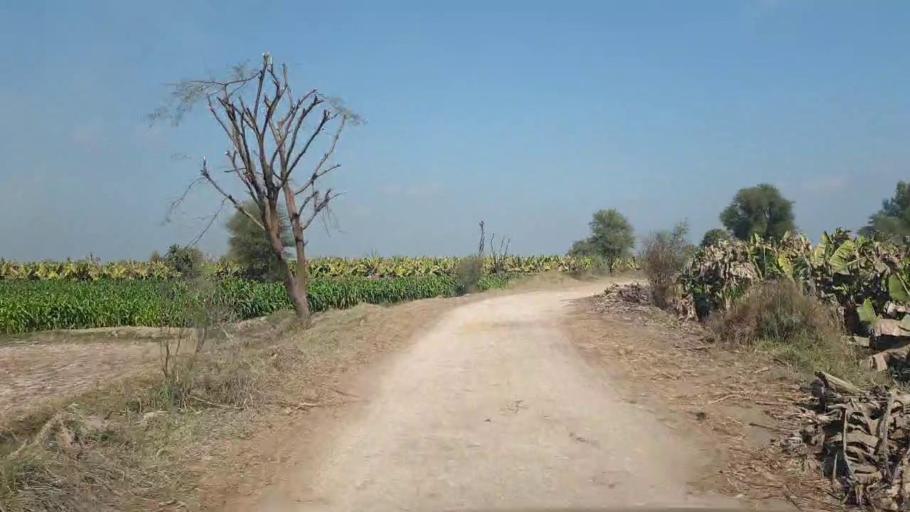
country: PK
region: Sindh
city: Shahdadpur
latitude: 25.9218
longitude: 68.5866
